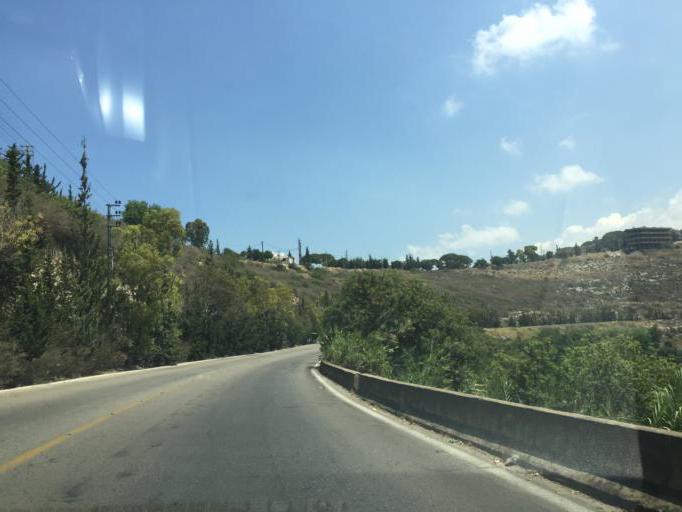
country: LB
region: Mont-Liban
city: Beit ed Dine
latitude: 33.7070
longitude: 35.4525
